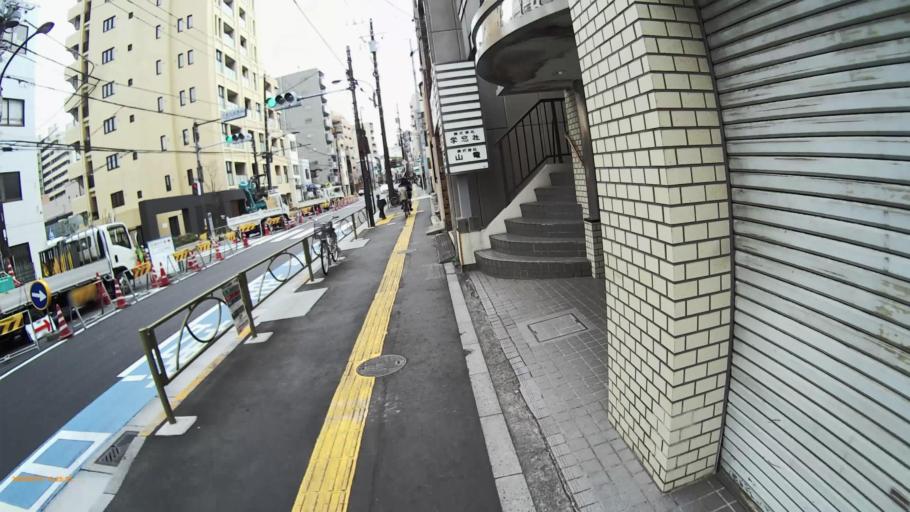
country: JP
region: Tokyo
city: Tokyo
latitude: 35.7177
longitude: 139.7559
